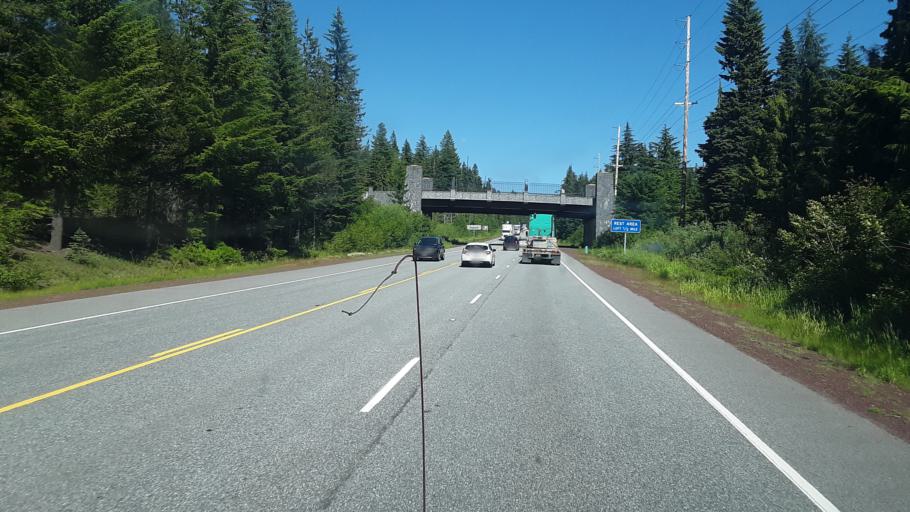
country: US
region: Oregon
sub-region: Clackamas County
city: Mount Hood Village
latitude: 45.3024
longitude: -121.7577
